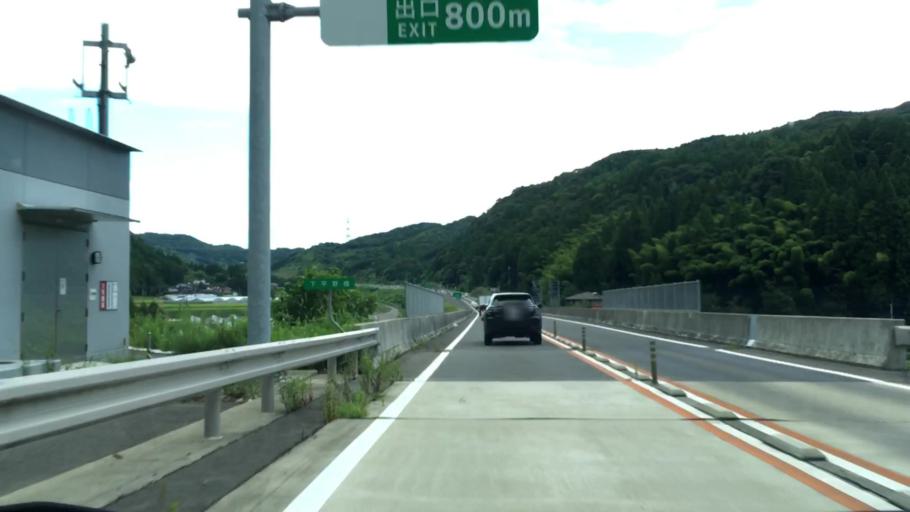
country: JP
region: Saga Prefecture
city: Karatsu
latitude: 33.3749
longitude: 129.9313
